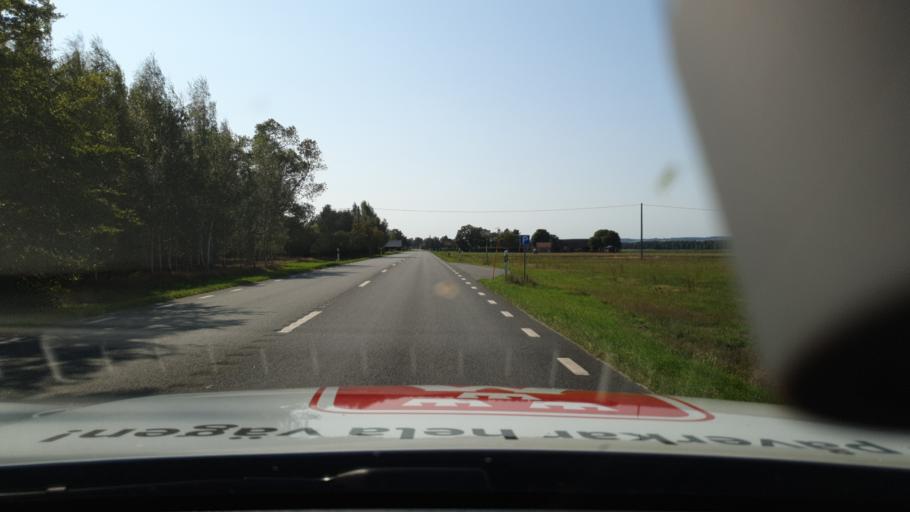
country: SE
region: Skane
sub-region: Kristianstads Kommun
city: Ahus
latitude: 55.8668
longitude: 14.2128
